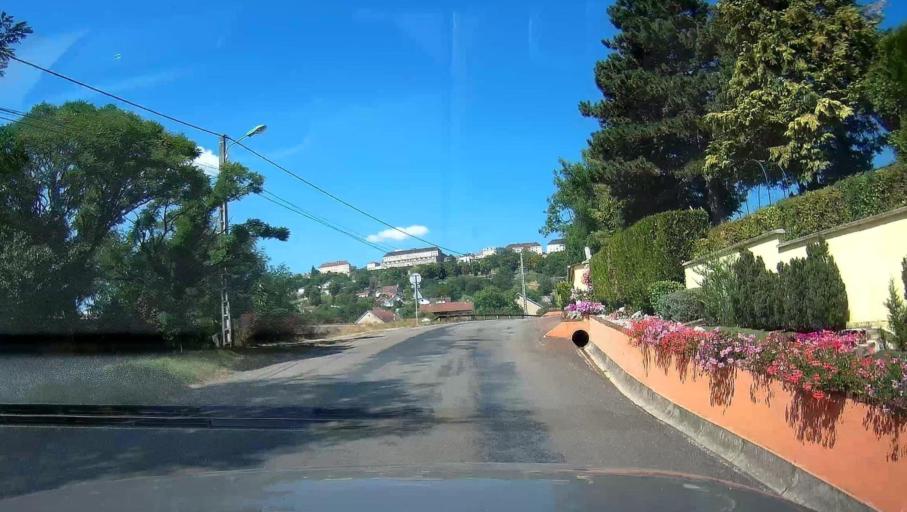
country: FR
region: Champagne-Ardenne
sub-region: Departement de la Haute-Marne
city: Langres
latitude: 47.8663
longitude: 5.3468
